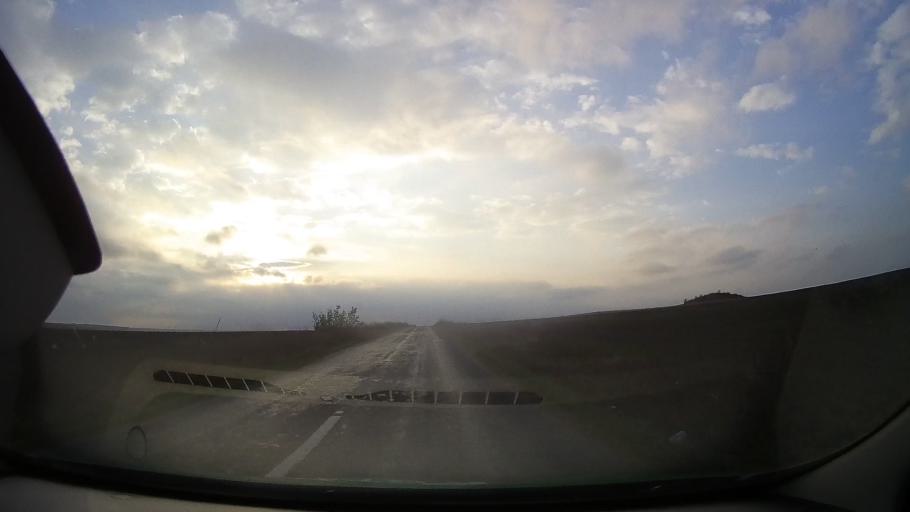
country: RO
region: Constanta
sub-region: Comuna Adamclisi
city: Adamclisi
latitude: 44.0172
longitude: 27.9021
